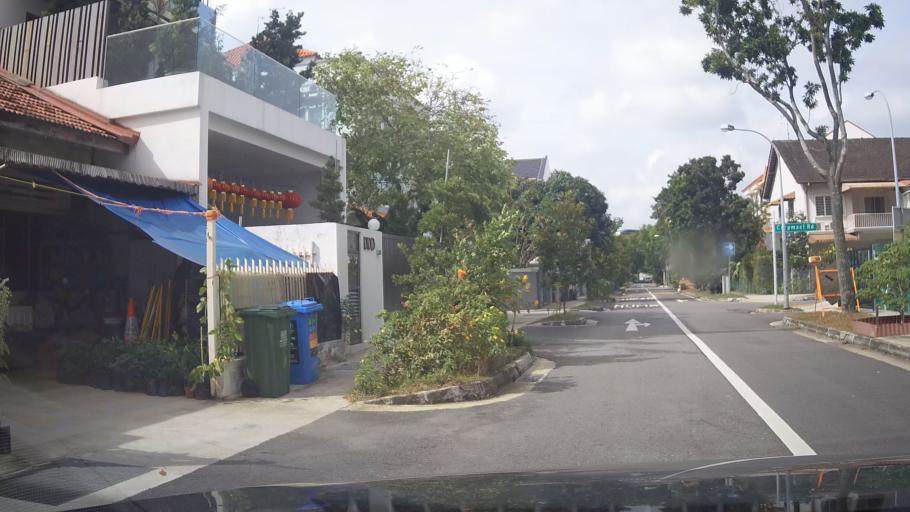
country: SG
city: Singapore
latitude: 1.3068
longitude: 103.9030
